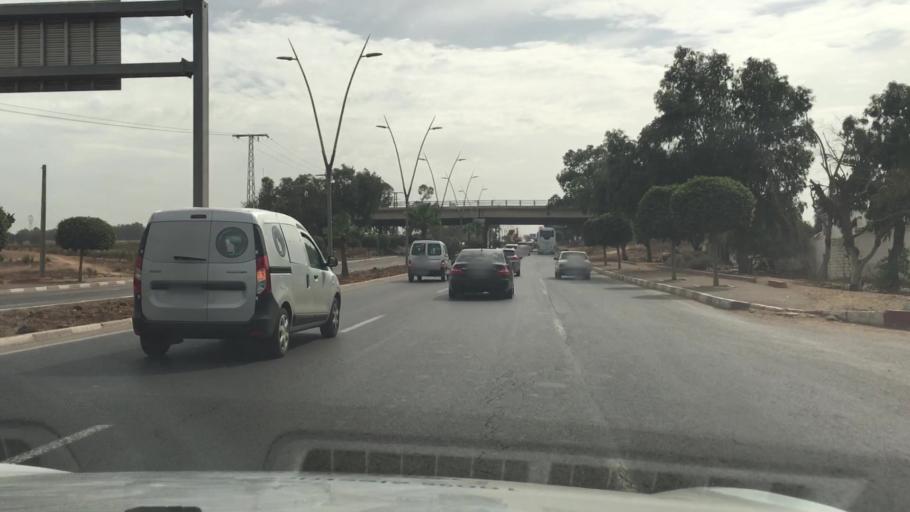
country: MA
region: Grand Casablanca
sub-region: Nouaceur
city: Bouskoura
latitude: 33.5132
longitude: -7.6311
